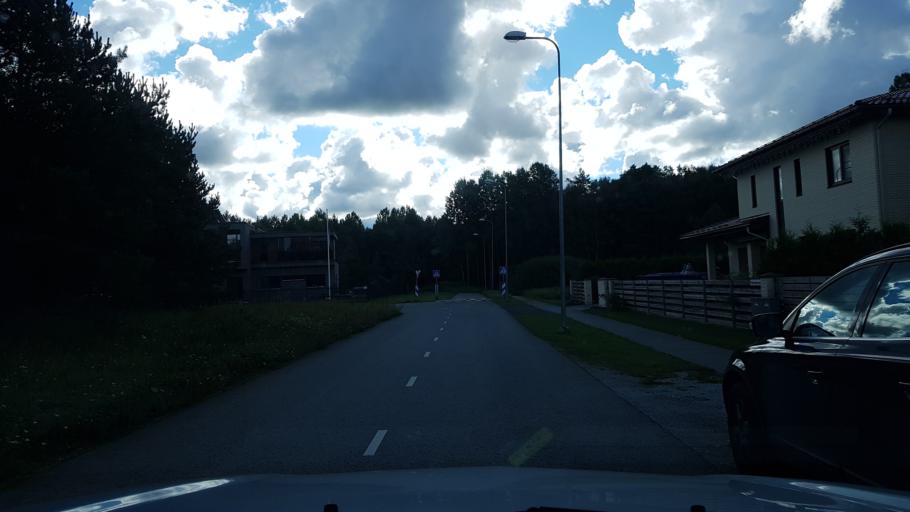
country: EE
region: Harju
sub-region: Tallinna linn
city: Tallinn
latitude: 59.3691
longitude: 24.7671
